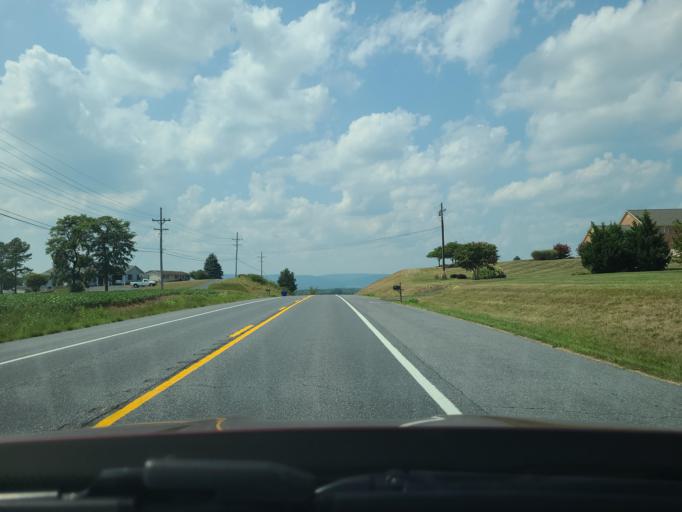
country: US
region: Maryland
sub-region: Frederick County
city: Woodsboro
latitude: 39.5573
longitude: -77.3429
